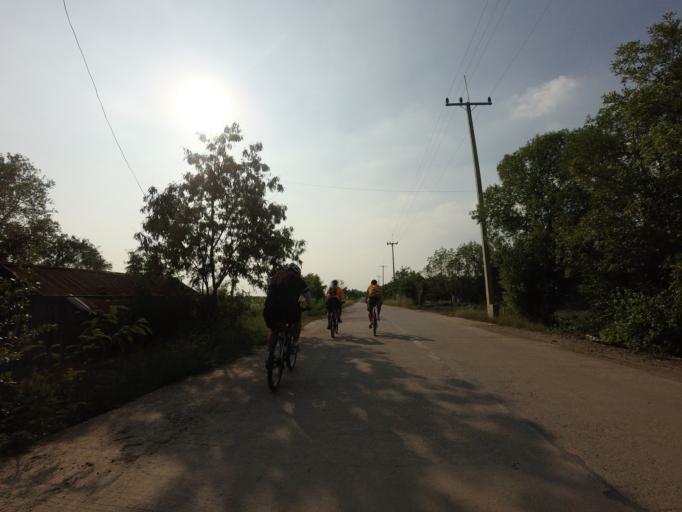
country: TH
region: Samut Sakhon
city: Samut Sakhon
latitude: 13.4984
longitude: 100.3407
